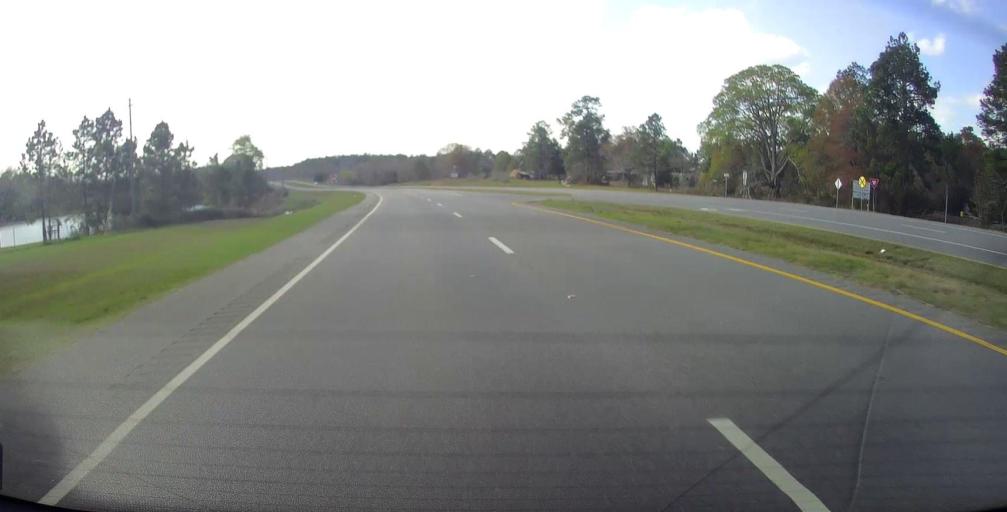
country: US
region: Georgia
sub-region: Telfair County
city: Helena
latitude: 32.1020
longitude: -82.9581
